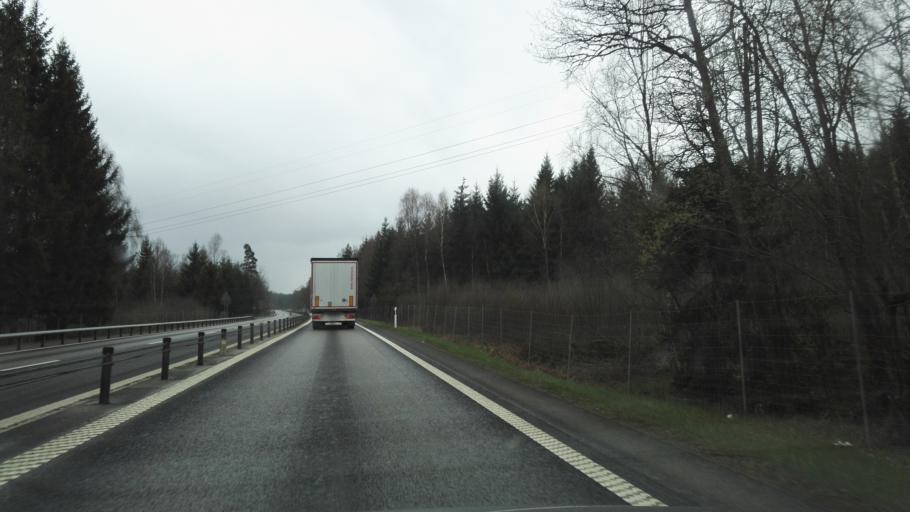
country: SE
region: Skane
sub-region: Osby Kommun
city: Osby
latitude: 56.3367
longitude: 14.0110
